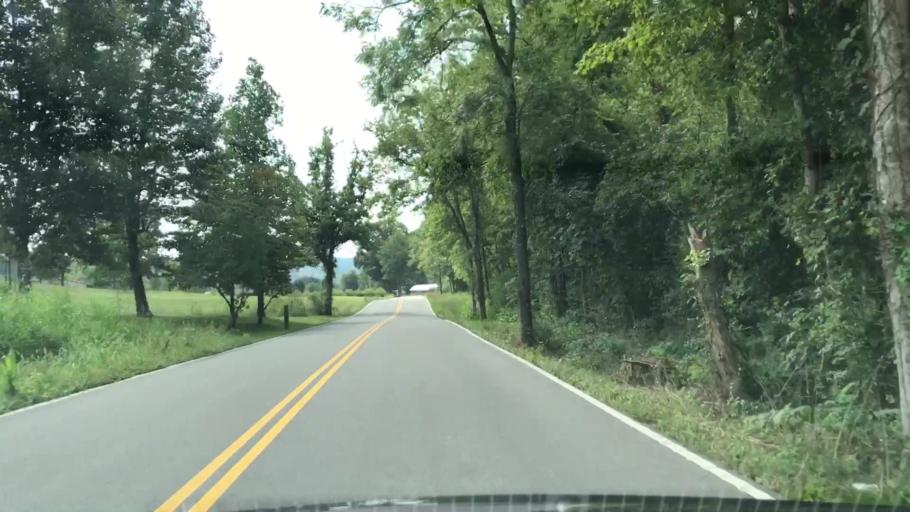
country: US
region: Tennessee
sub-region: Trousdale County
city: Hartsville
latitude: 36.4810
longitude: -86.1864
